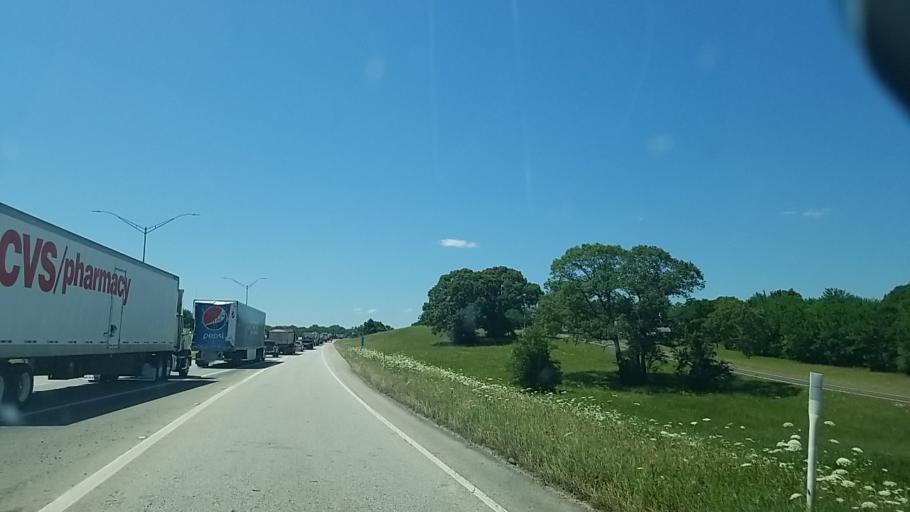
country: US
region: Texas
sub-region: Leon County
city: Buffalo
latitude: 31.4543
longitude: -96.0788
